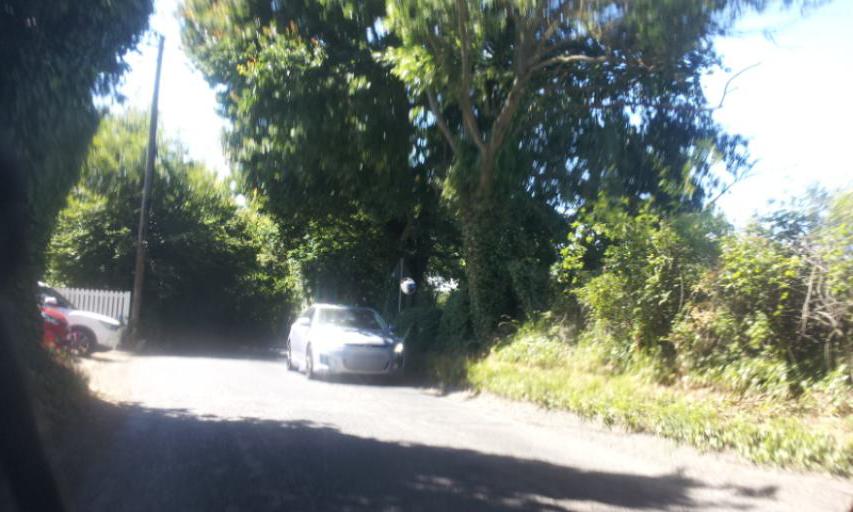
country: GB
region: England
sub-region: Kent
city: Newington
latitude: 51.3748
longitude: 0.6801
